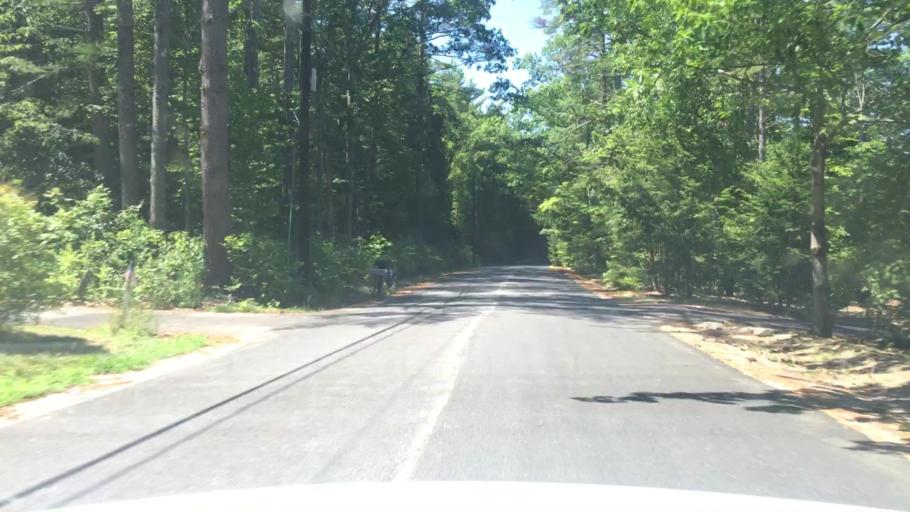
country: US
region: New Hampshire
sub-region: Merrimack County
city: Hopkinton
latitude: 43.2338
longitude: -71.6417
